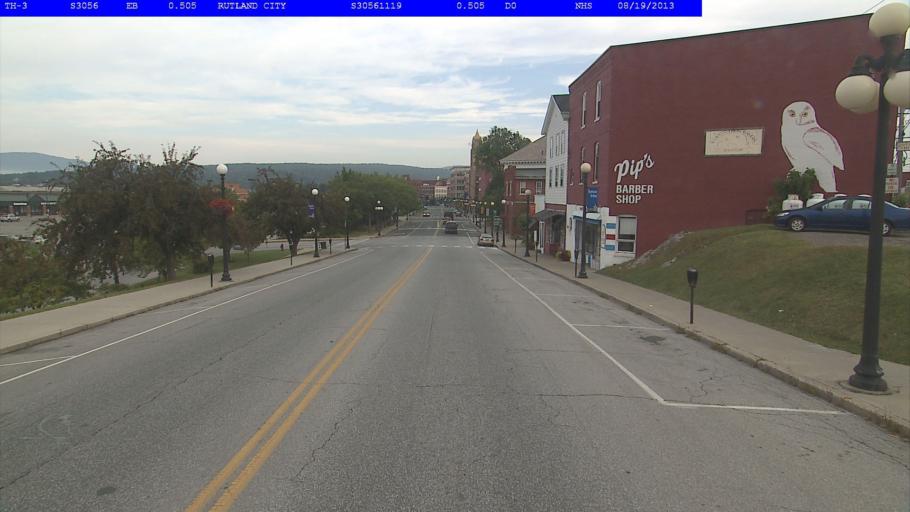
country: US
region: Vermont
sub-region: Rutland County
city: Rutland
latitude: 43.6043
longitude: -72.9773
